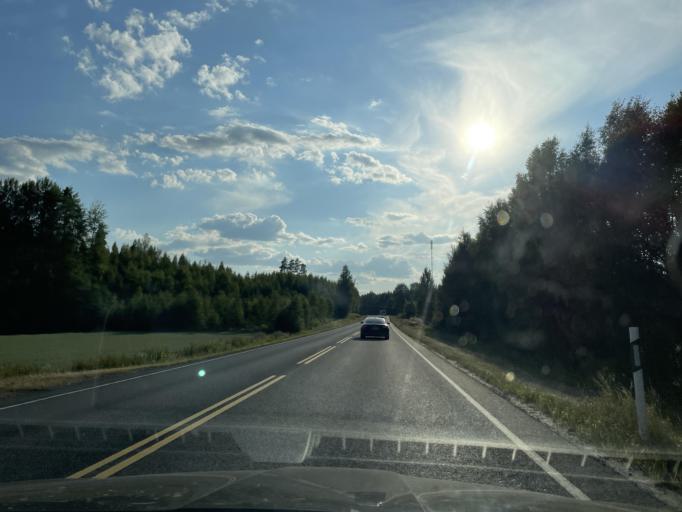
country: FI
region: Haeme
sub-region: Haemeenlinna
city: Tuulos
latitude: 61.0988
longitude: 24.8319
